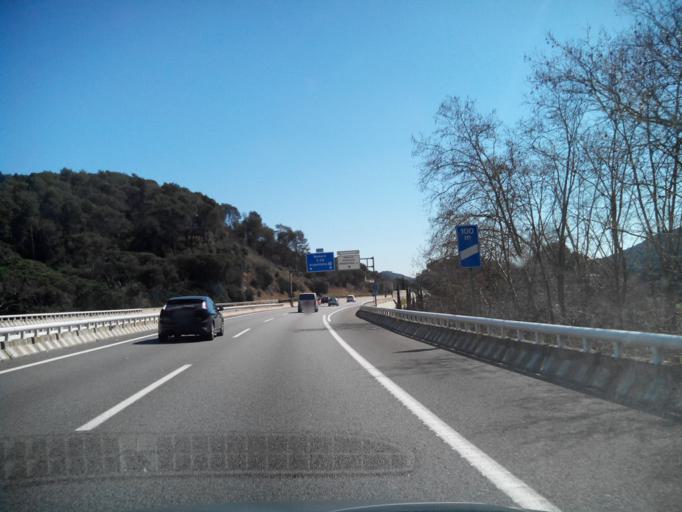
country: ES
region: Catalonia
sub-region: Provincia de Barcelona
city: Argentona
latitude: 41.5785
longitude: 2.3818
